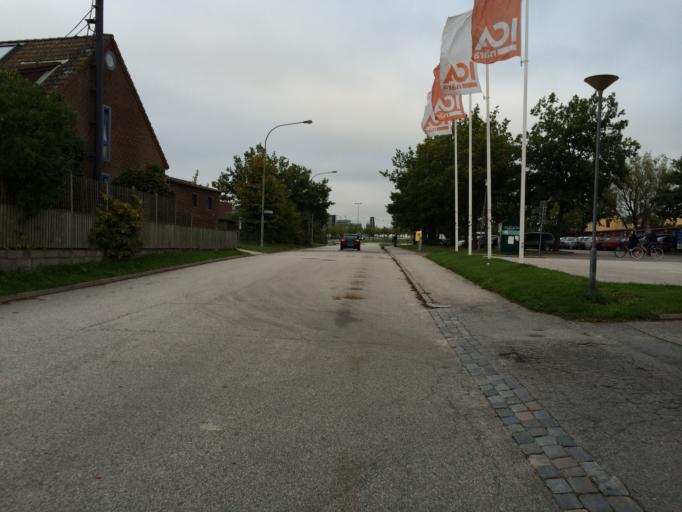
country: SE
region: Skane
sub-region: Lunds Kommun
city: Lund
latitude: 55.7142
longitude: 13.2298
